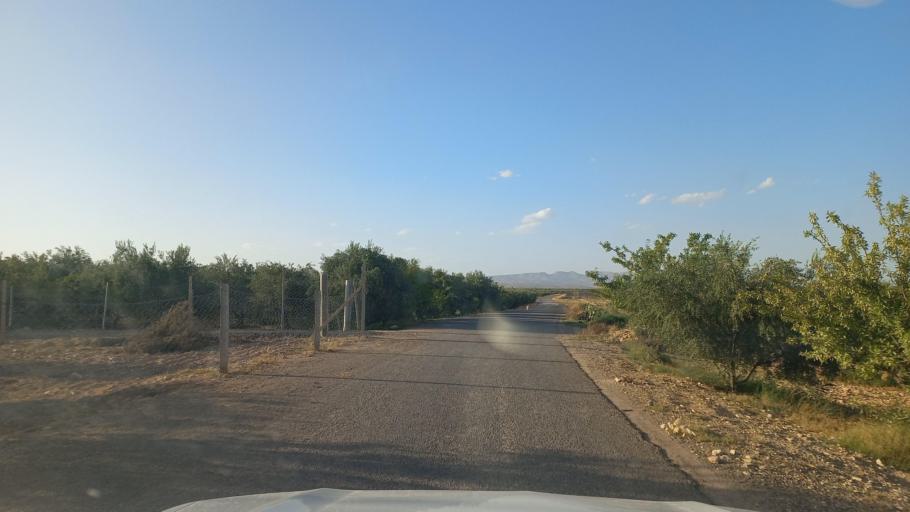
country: TN
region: Al Qasrayn
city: Kasserine
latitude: 35.2804
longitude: 9.0275
